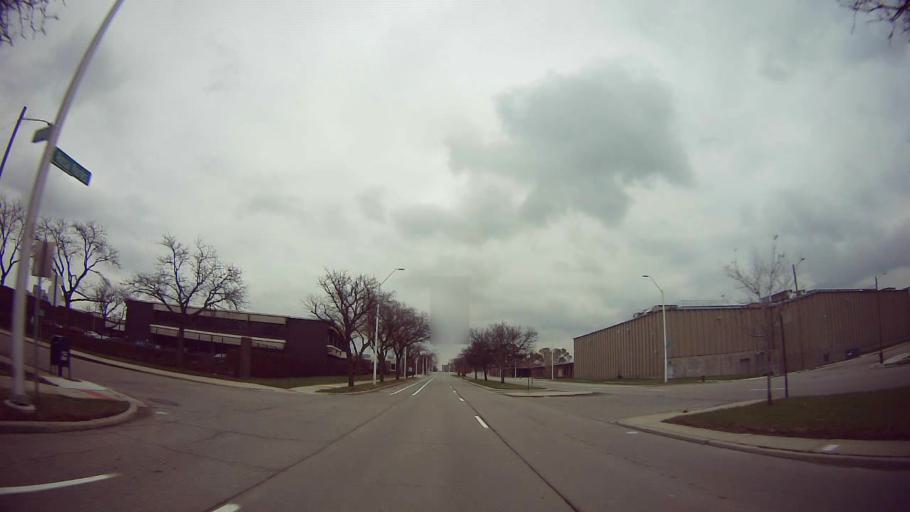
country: US
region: Michigan
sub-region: Wayne County
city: Detroit
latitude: 42.3262
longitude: -83.0688
